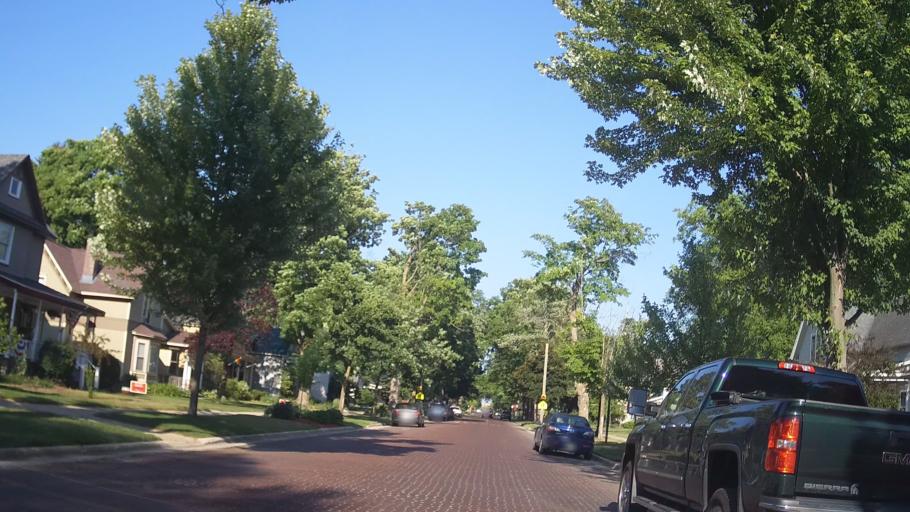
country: US
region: Michigan
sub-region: Grand Traverse County
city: Traverse City
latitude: 44.7593
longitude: -85.6304
